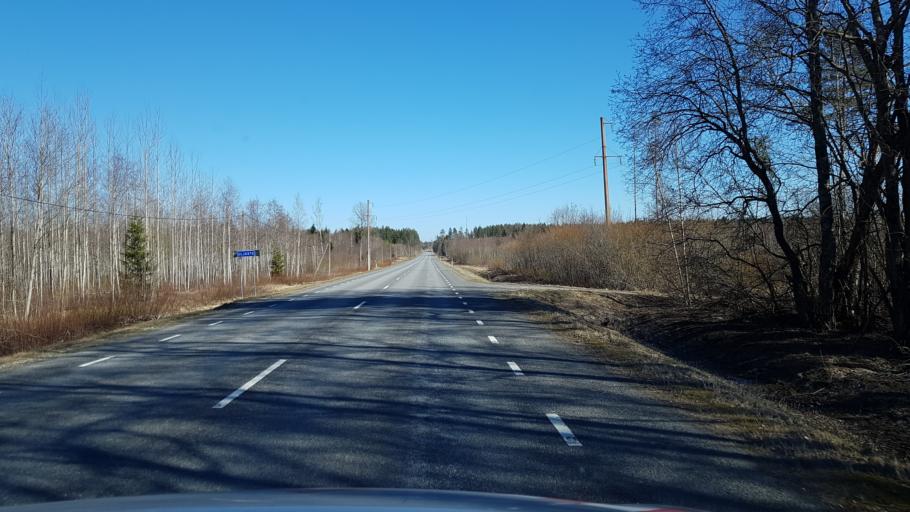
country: EE
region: Ida-Virumaa
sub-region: Aseri vald
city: Aseri
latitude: 59.3536
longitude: 26.7376
